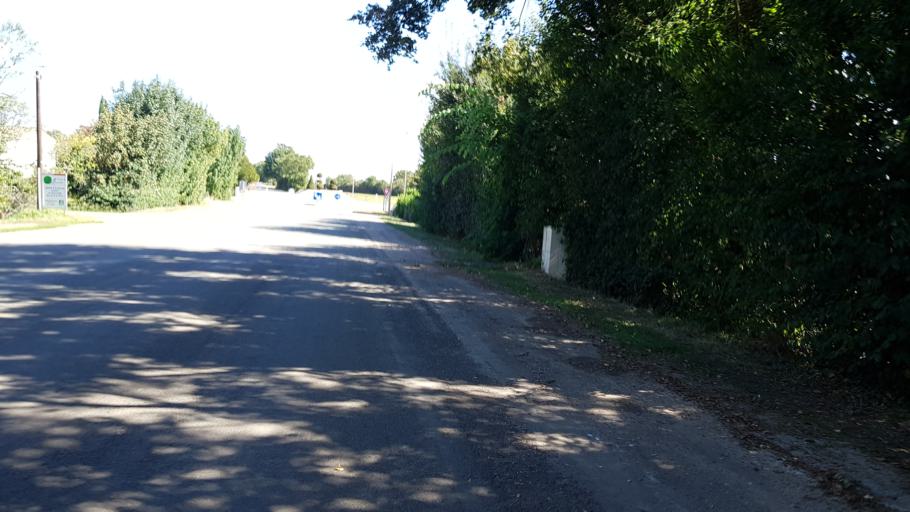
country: FR
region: Poitou-Charentes
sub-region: Departement des Deux-Sevres
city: Vouille
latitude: 46.3125
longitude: -0.3745
